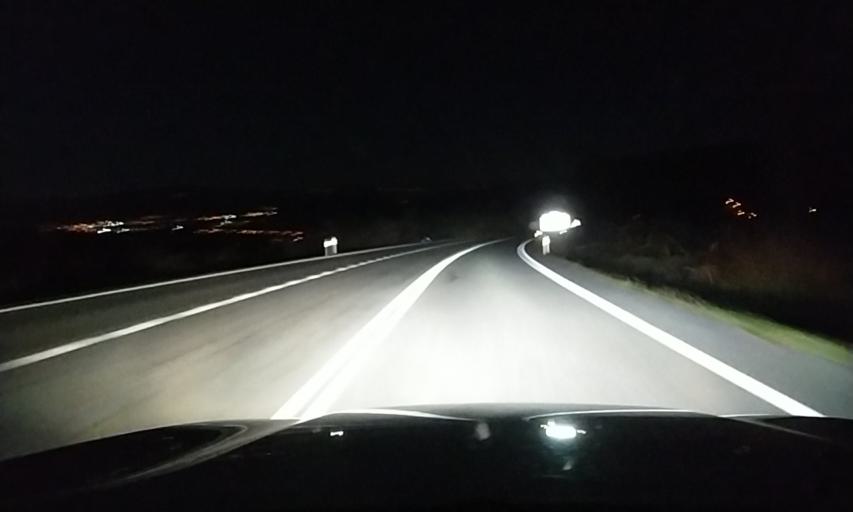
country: ES
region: Galicia
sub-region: Provincia de Ourense
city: Cualedro
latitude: 41.9754
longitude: -7.5205
